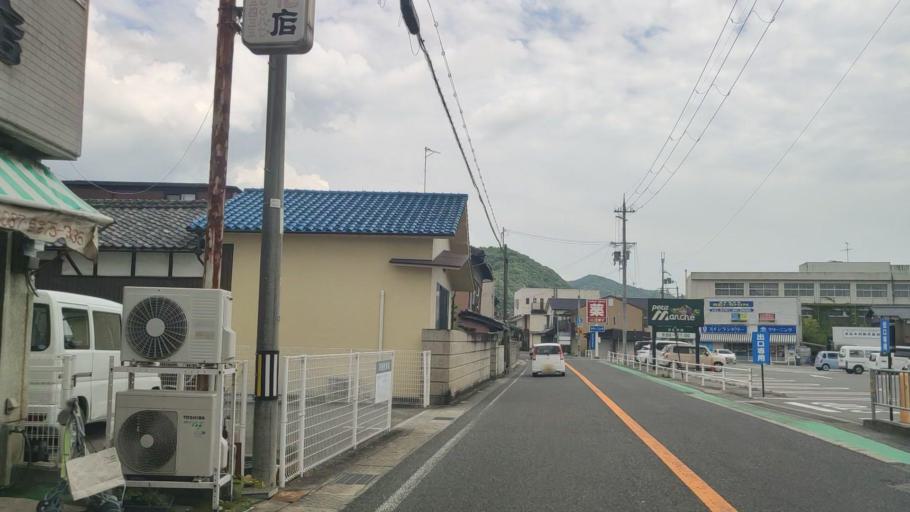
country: JP
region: Hyogo
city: Tatsunocho-tominaga
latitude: 34.9196
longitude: 134.5461
